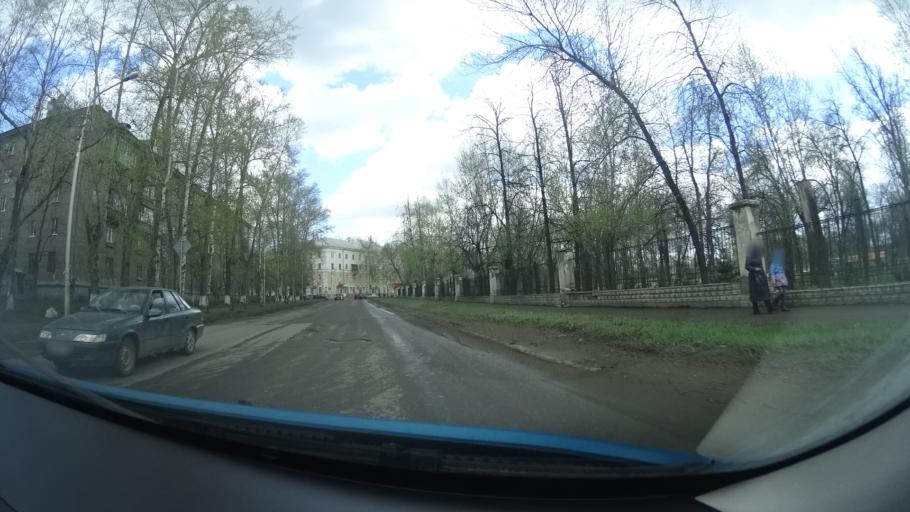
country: RU
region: Bashkortostan
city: Ufa
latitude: 54.8192
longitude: 56.0902
